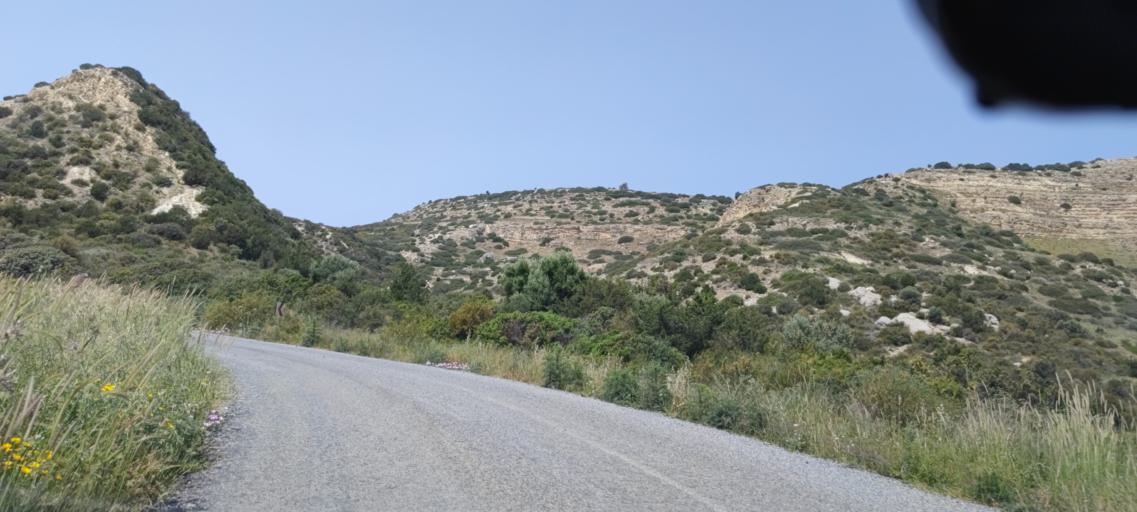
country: CY
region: Ammochostos
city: Rizokarpaso
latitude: 35.5247
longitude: 34.3219
